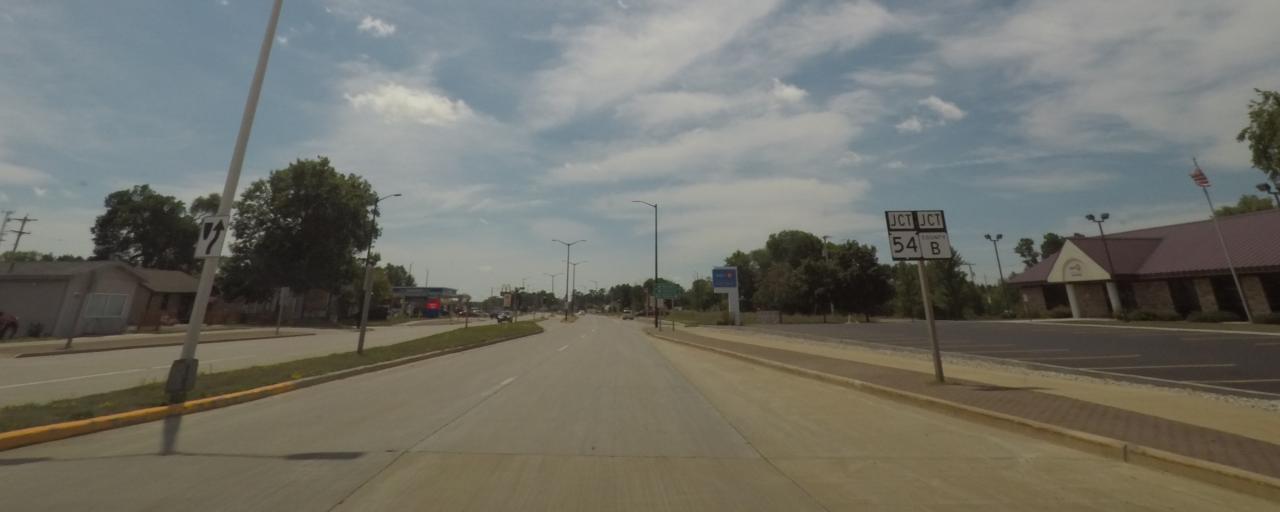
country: US
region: Wisconsin
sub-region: Portage County
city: Plover
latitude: 44.4553
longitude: -89.5441
